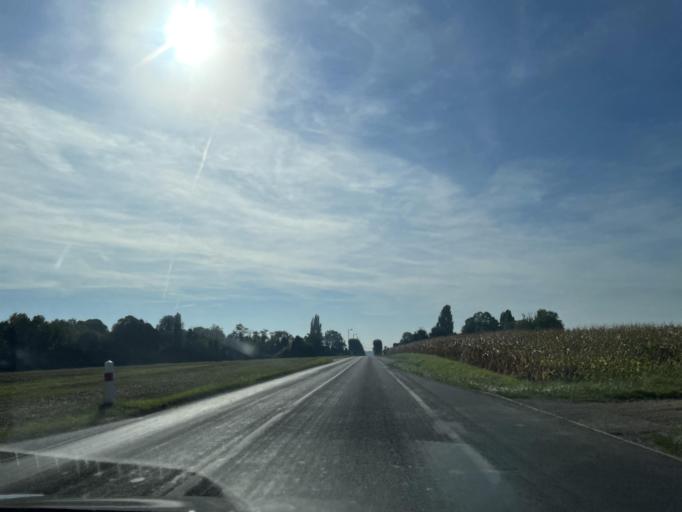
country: FR
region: Ile-de-France
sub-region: Departement de Seine-et-Marne
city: Coulommiers
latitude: 48.8302
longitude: 3.0873
